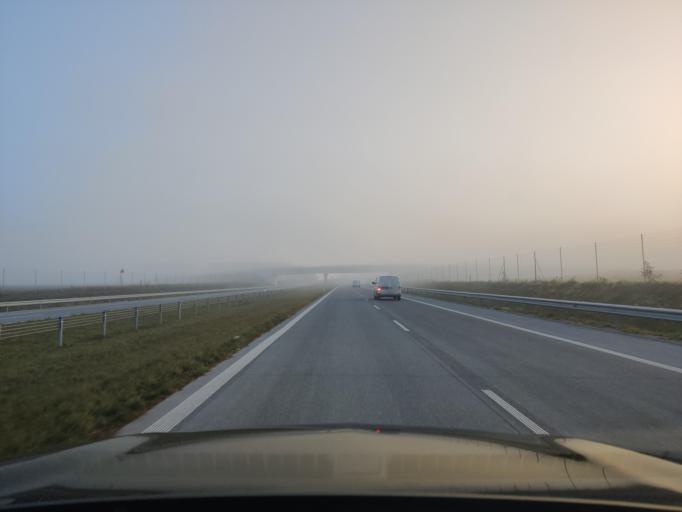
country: PL
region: Masovian Voivodeship
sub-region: Powiat mlawski
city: Strzegowo
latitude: 52.9725
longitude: 20.3245
